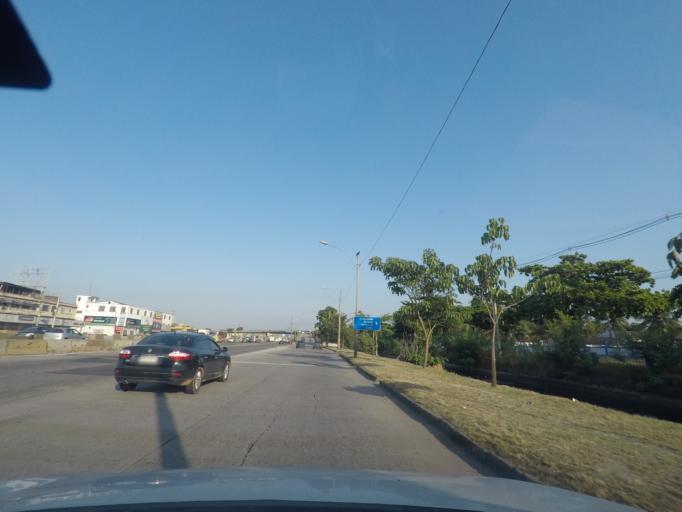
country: BR
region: Rio de Janeiro
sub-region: Duque De Caxias
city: Duque de Caxias
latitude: -22.8284
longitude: -43.2722
